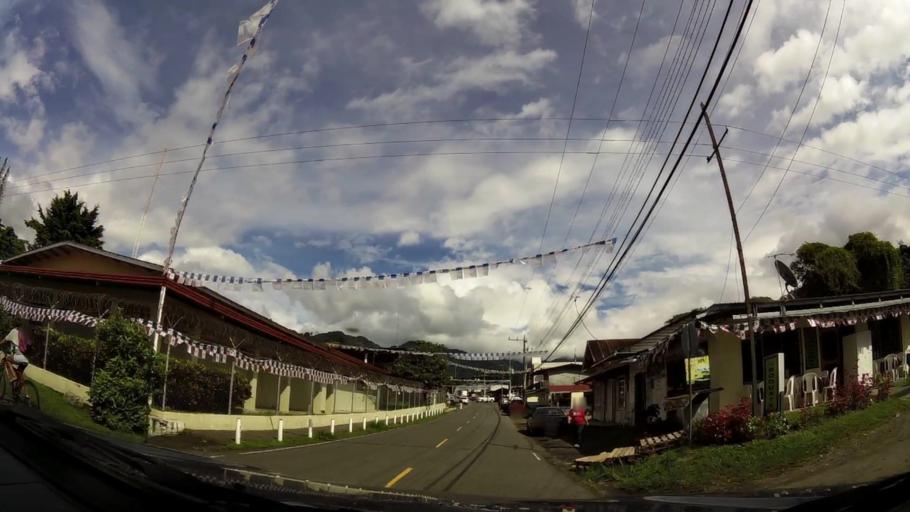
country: PA
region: Chiriqui
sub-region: Distrito Boquete
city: Boquete
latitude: 8.7752
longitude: -82.4314
